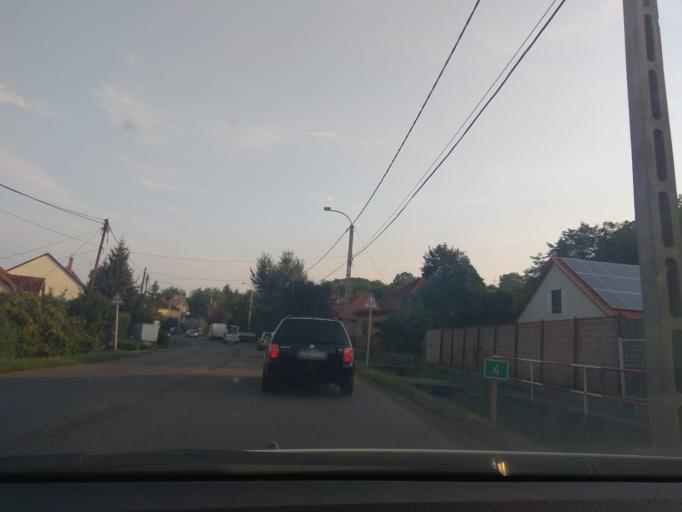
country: HU
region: Heves
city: Andornaktalya
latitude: 47.8639
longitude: 20.4073
